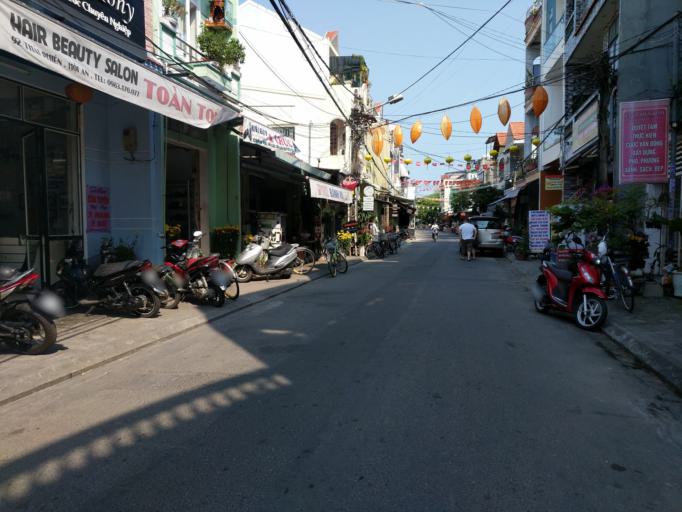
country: VN
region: Quang Nam
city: Hoi An
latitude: 15.8818
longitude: 108.3266
